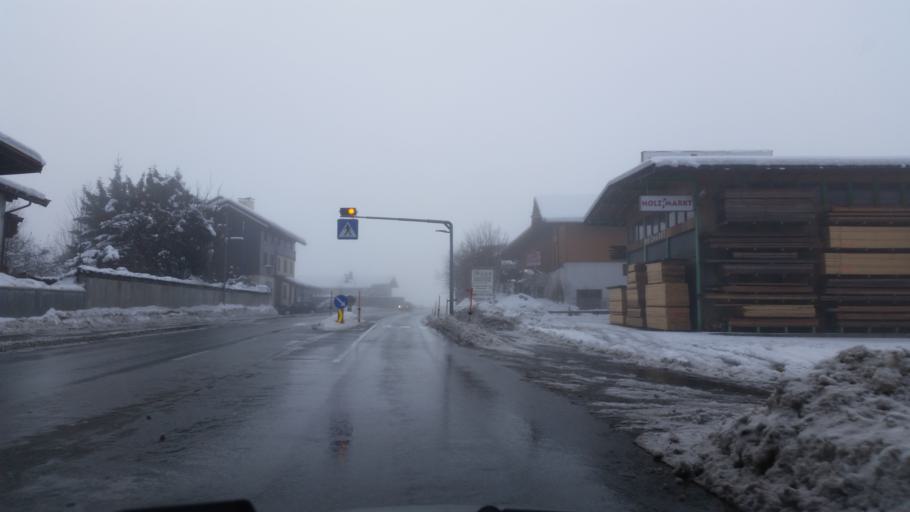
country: AT
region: Tyrol
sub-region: Politischer Bezirk Kitzbuhel
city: Kirchdorf in Tirol
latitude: 47.5433
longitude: 12.4481
